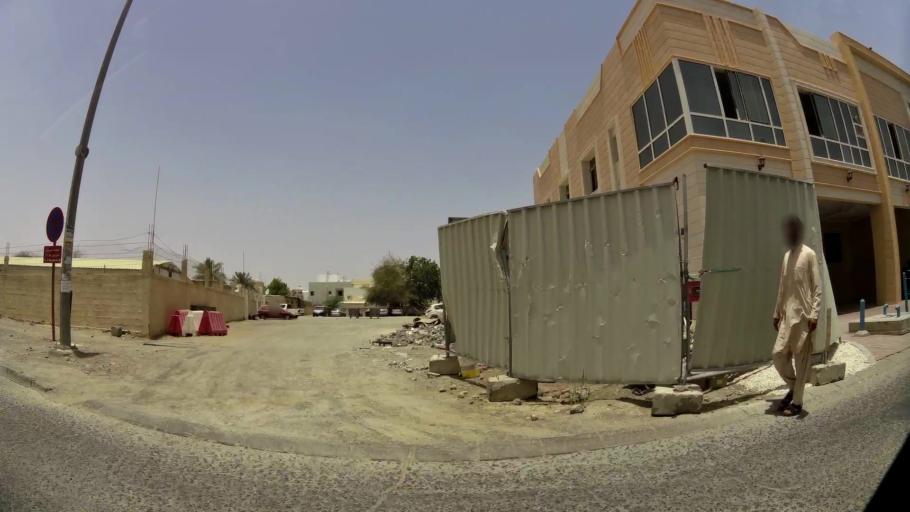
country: AE
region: Abu Dhabi
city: Al Ain
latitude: 24.2108
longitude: 55.7545
